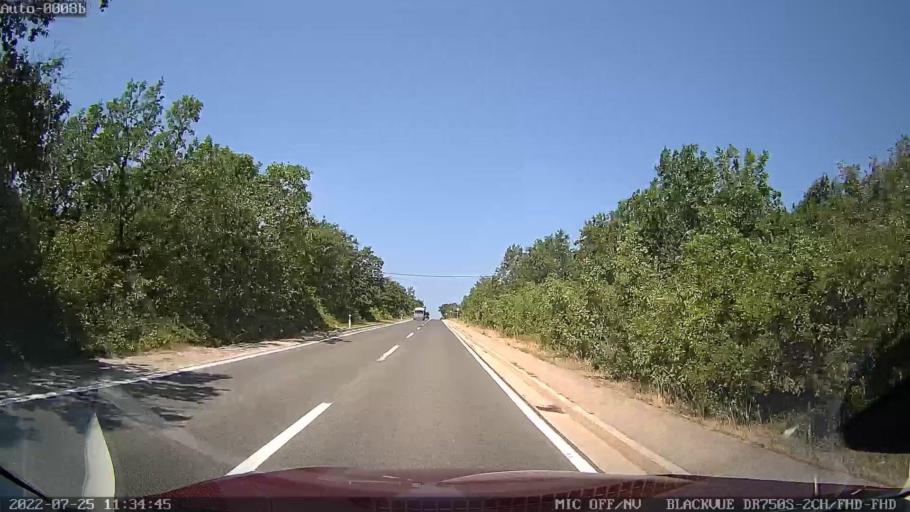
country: HR
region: Zadarska
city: Posedarje
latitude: 44.2312
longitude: 15.4184
